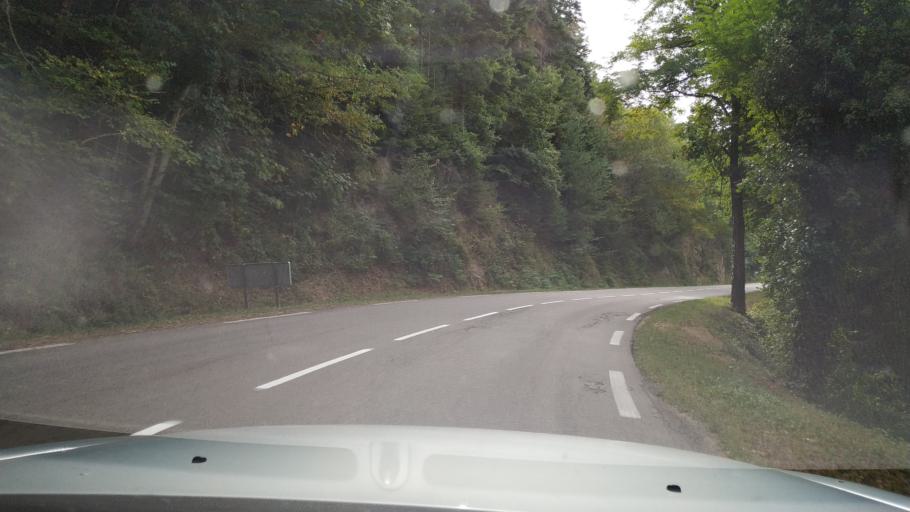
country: FR
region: Rhone-Alpes
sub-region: Departement de l'Ardeche
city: Desaignes
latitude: 44.9864
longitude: 4.5406
